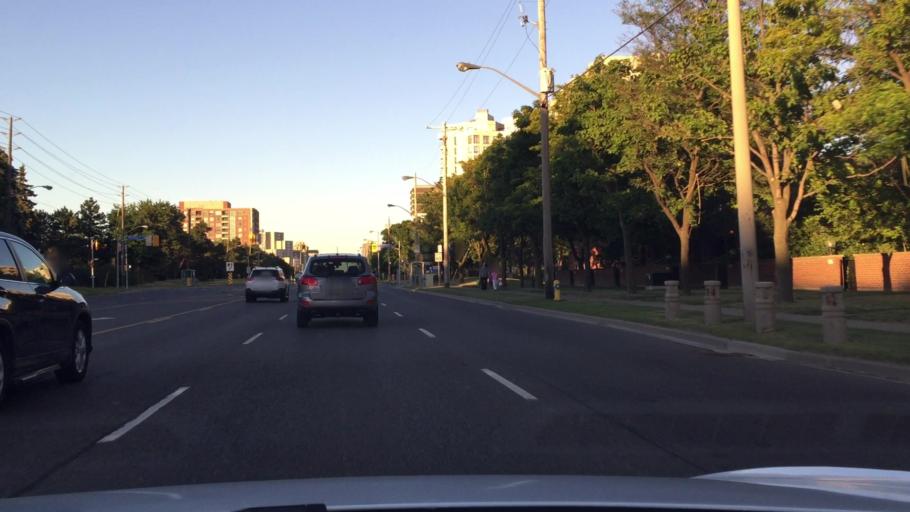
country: CA
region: Ontario
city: Concord
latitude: 43.7905
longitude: -79.4543
